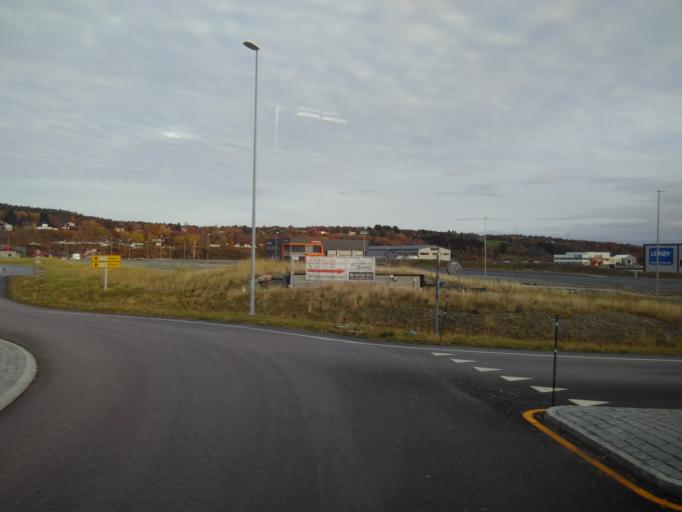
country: NO
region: Sor-Trondelag
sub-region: Hitra
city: Fillan
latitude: 63.5190
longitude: 9.1105
